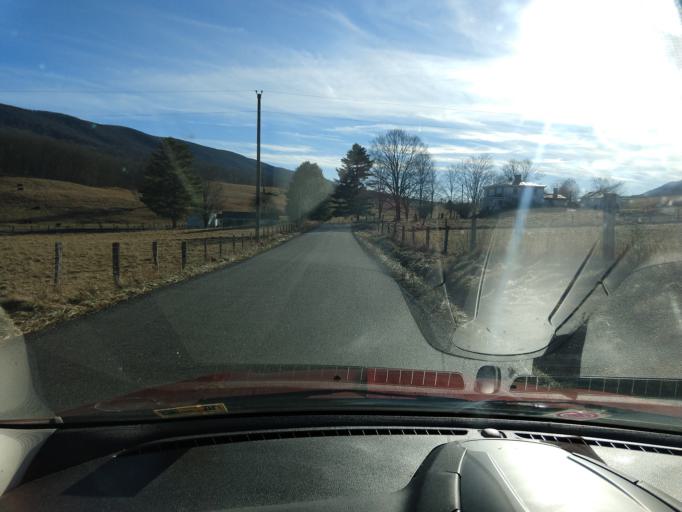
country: US
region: Virginia
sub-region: Highland County
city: Monterey
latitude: 38.3770
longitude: -79.6649
